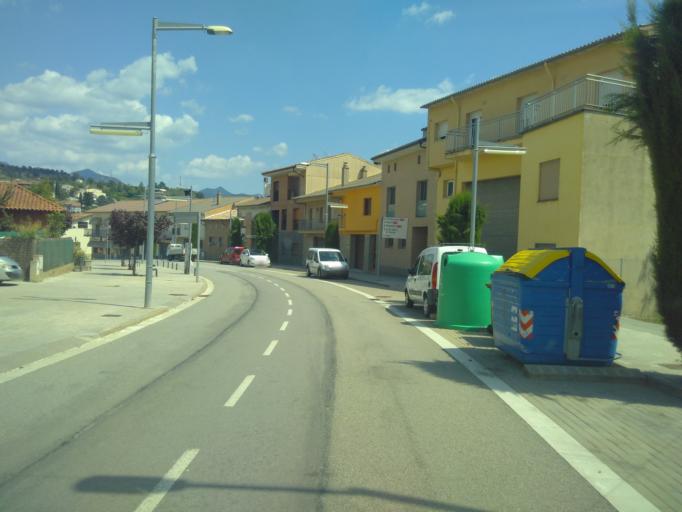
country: ES
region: Catalonia
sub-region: Provincia de Barcelona
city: Montesquiu
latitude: 42.0992
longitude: 2.2150
